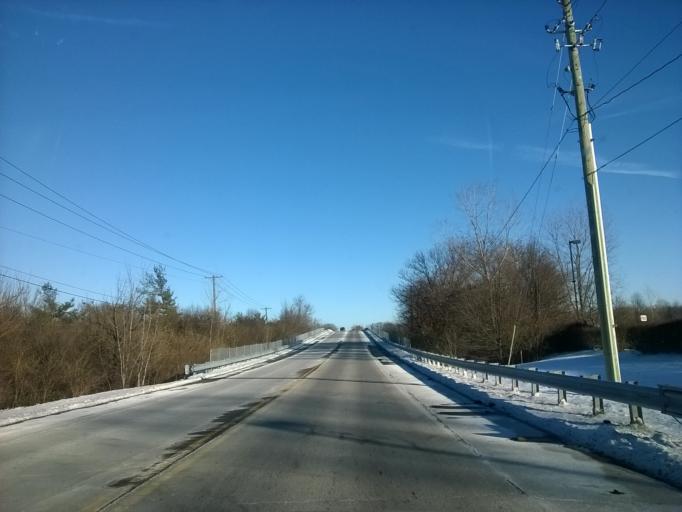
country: US
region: Indiana
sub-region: Marion County
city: Meridian Hills
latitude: 39.9268
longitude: -86.1812
